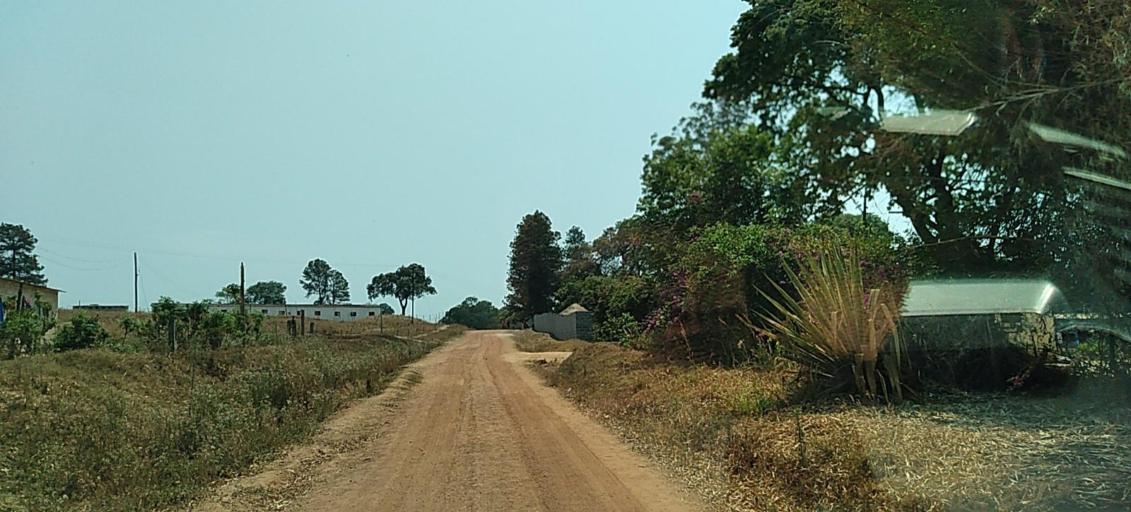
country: ZM
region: Copperbelt
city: Chingola
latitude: -12.6258
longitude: 27.9403
